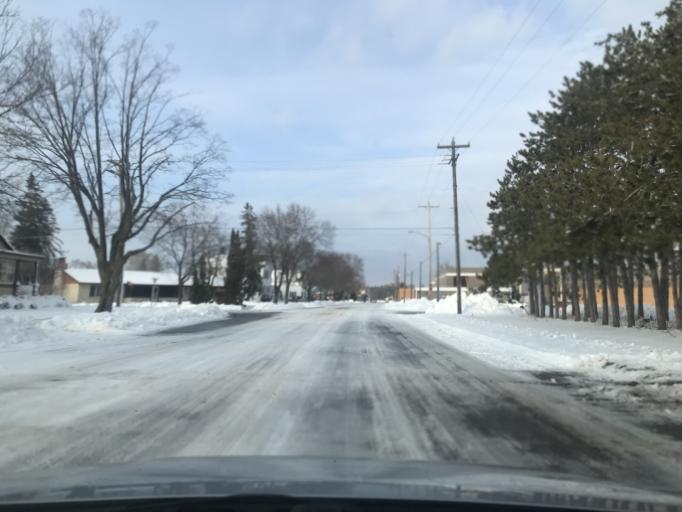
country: US
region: Wisconsin
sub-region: Marinette County
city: Peshtigo
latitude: 45.0506
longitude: -87.7490
